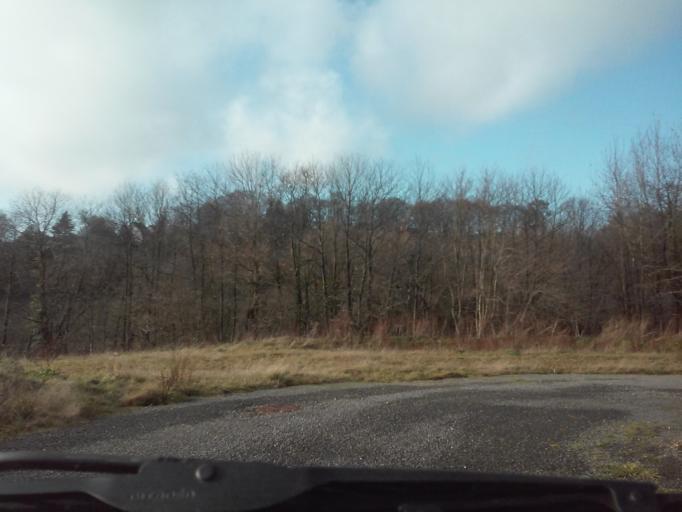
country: FR
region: Brittany
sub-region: Departement d'Ille-et-Vilaine
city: Fougeres
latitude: 48.3631
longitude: -1.1984
